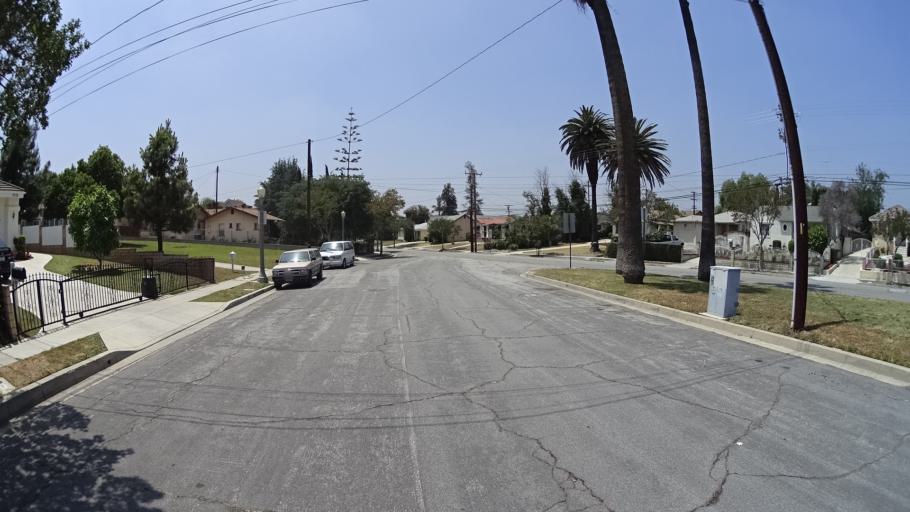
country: US
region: California
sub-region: Los Angeles County
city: Belvedere
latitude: 34.0658
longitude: -118.1530
